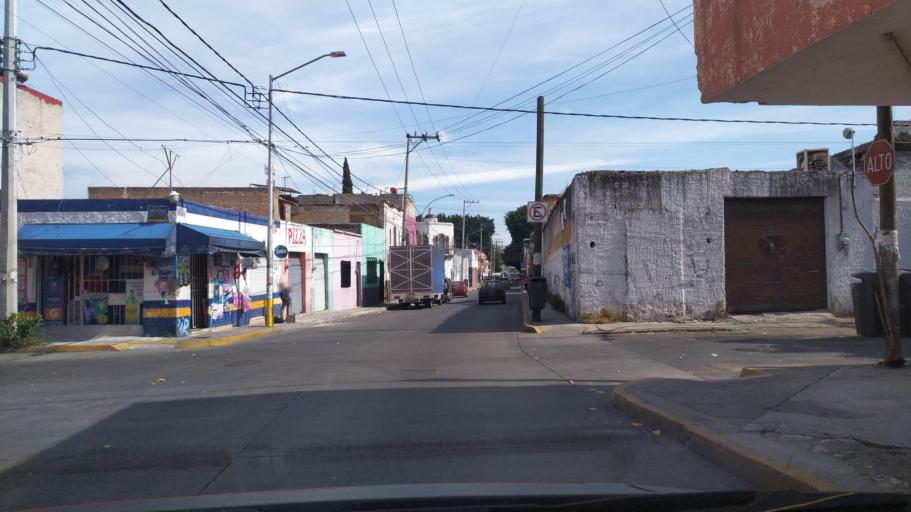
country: MX
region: Jalisco
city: Tlaquepaque
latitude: 20.6822
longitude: -103.3324
